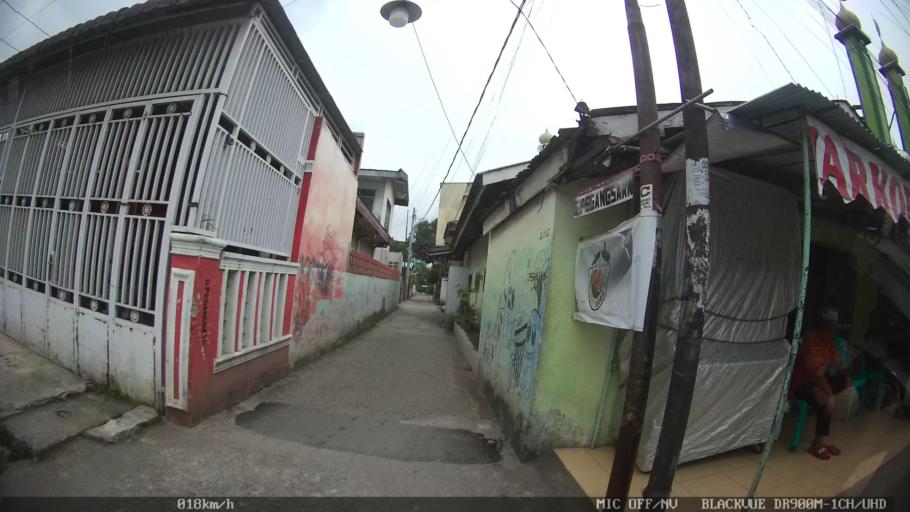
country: ID
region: North Sumatra
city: Medan
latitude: 3.5785
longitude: 98.7020
